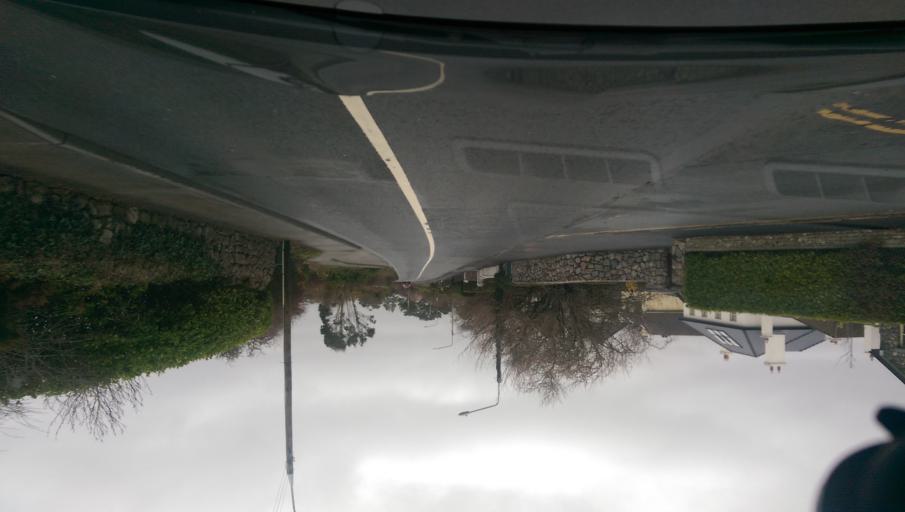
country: IE
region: Connaught
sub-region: County Galway
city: Bearna
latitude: 53.2647
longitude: -9.1005
